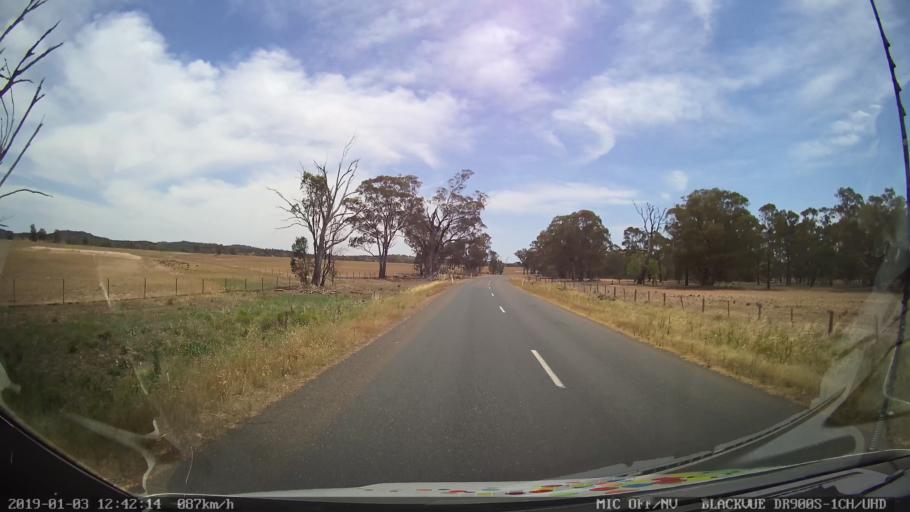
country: AU
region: New South Wales
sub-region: Weddin
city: Grenfell
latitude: -33.7897
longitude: 148.2122
